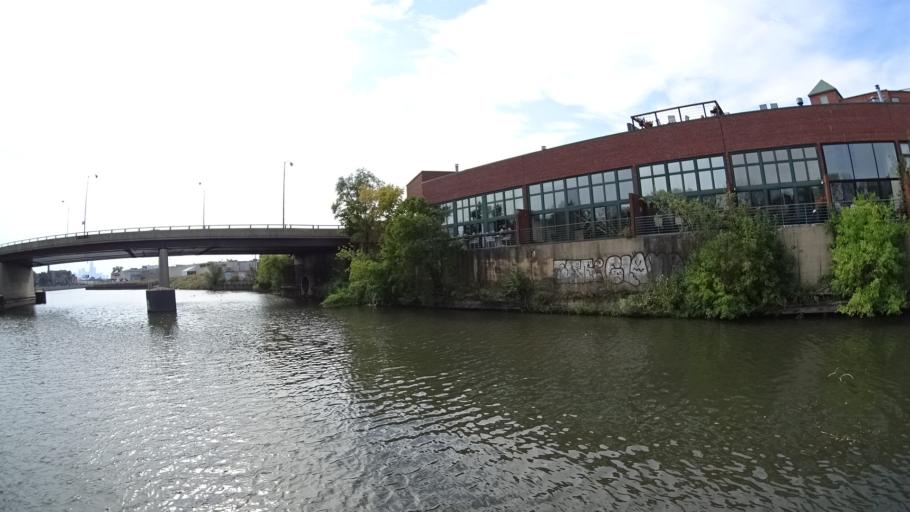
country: US
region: Illinois
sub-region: Cook County
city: Lincolnwood
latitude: 41.9328
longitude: -87.6832
